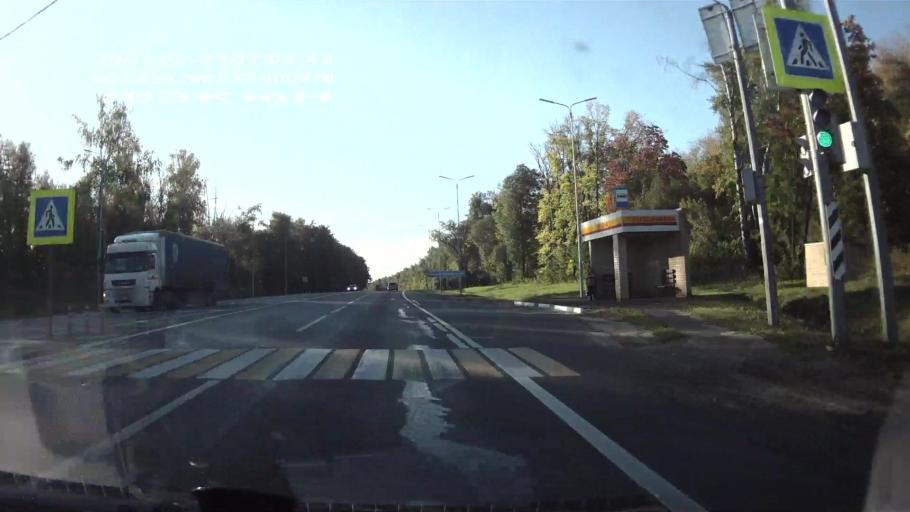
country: RU
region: Chuvashia
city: Tsivil'sk
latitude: 55.9231
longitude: 47.4005
